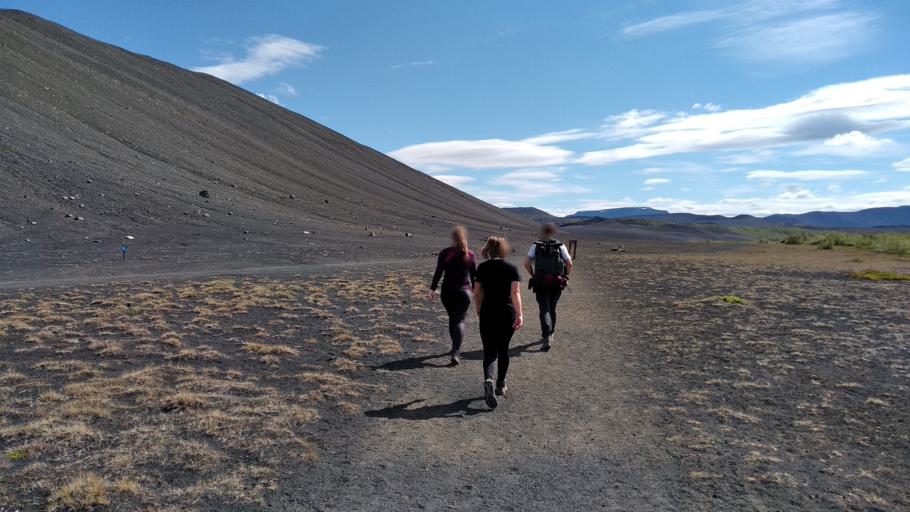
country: IS
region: Northeast
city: Laugar
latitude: 65.5989
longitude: -16.8864
